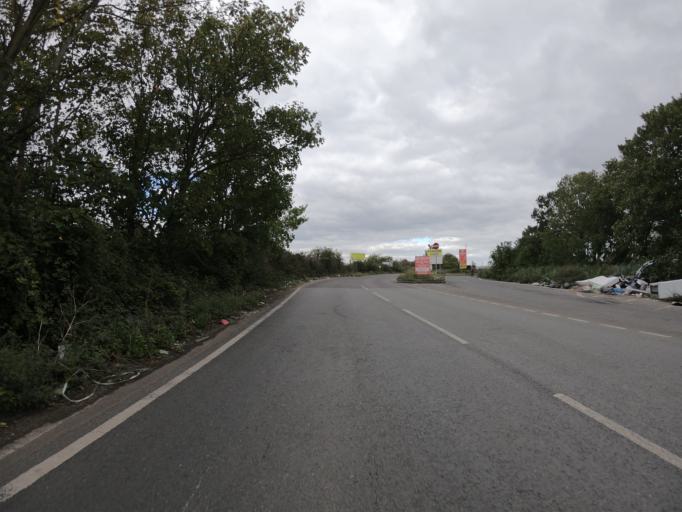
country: GB
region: England
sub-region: Greater London
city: Erith
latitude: 51.4763
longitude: 0.2086
